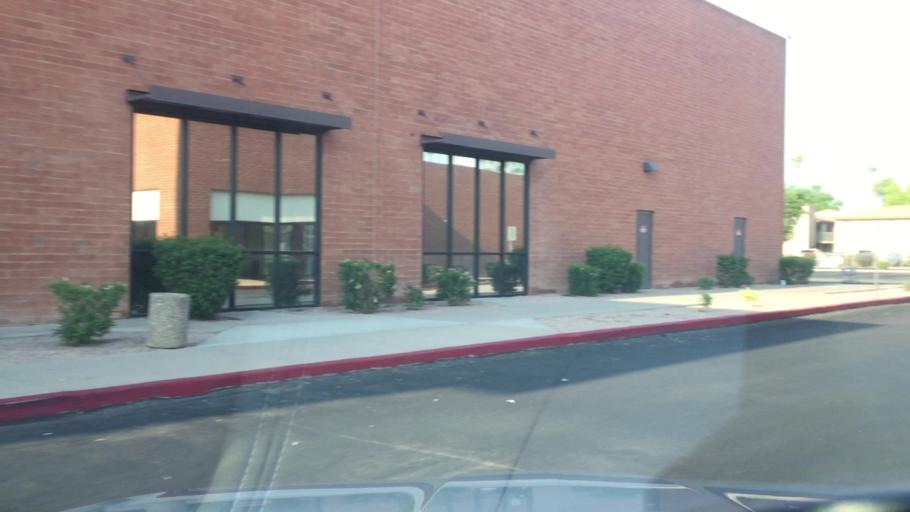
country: US
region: Arizona
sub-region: Maricopa County
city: Mesa
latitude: 33.3943
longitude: -111.8538
